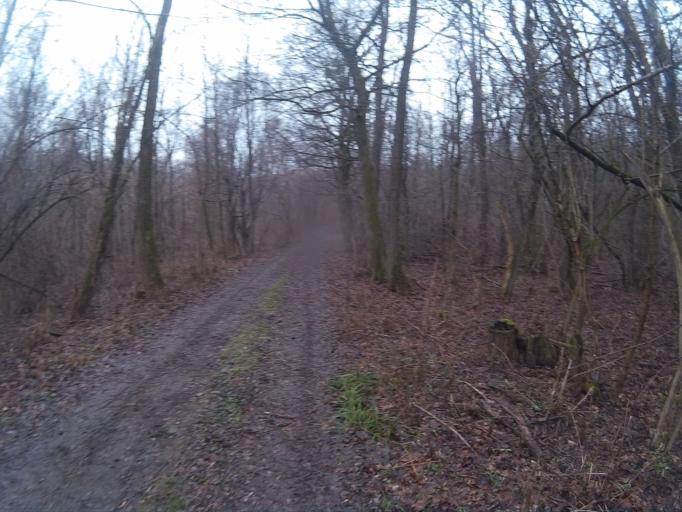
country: HU
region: Komarom-Esztergom
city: Nyergesujfalu
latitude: 47.7225
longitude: 18.5852
